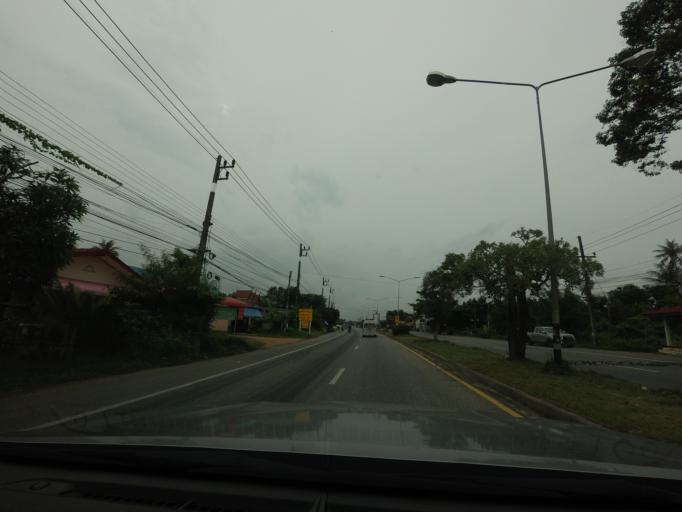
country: TH
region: Songkhla
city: Singhanakhon
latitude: 7.2629
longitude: 100.5234
